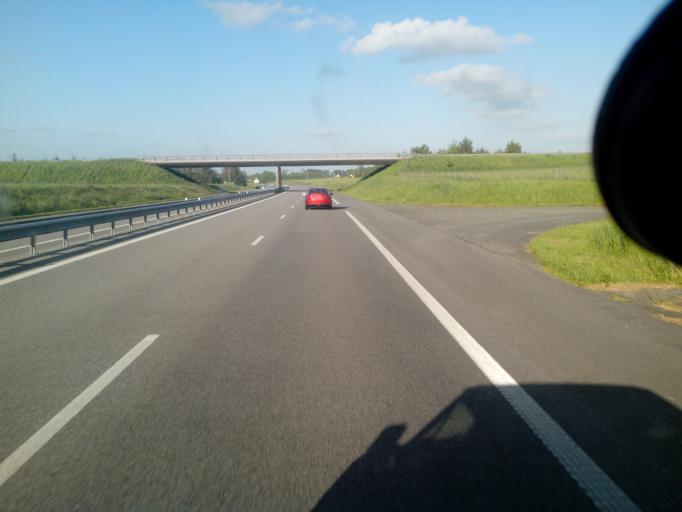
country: FR
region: Haute-Normandie
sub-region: Departement de la Seine-Maritime
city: Yerville
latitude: 49.6572
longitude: 0.8988
